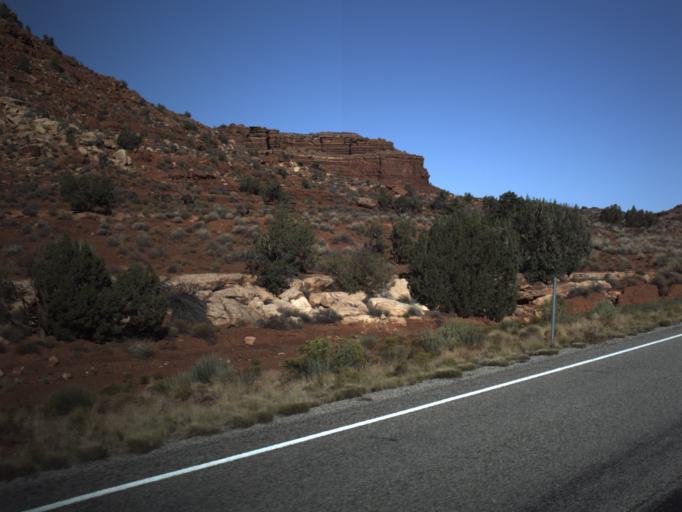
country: US
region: Utah
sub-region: San Juan County
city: Blanding
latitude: 37.7532
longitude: -110.2804
